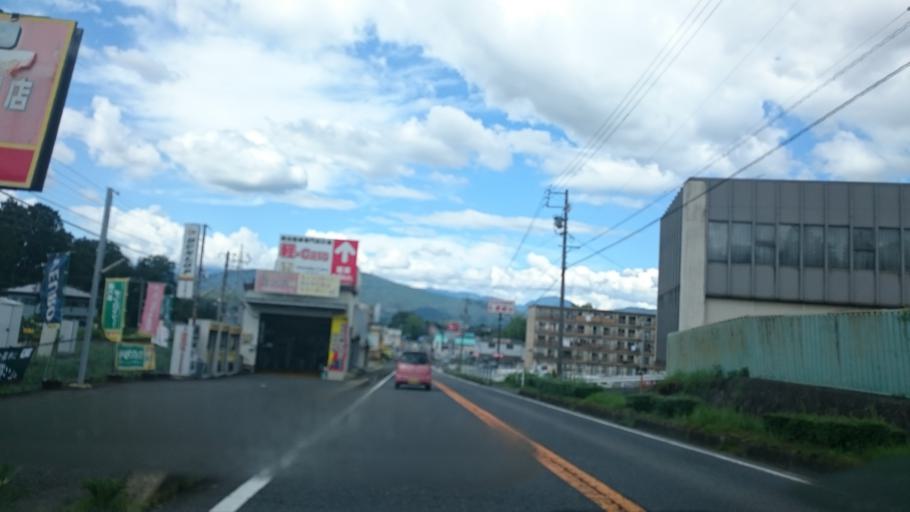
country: JP
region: Gifu
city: Nakatsugawa
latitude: 35.4816
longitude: 137.4856
